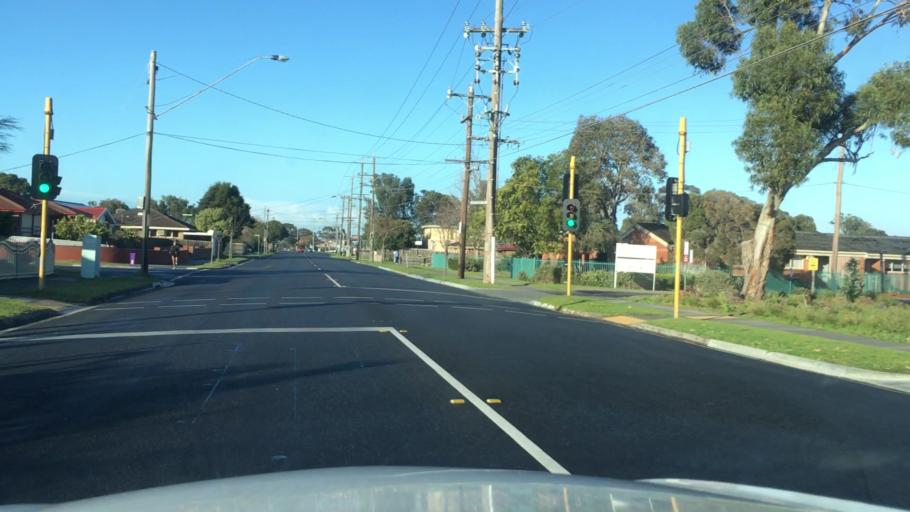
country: AU
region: Victoria
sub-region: Greater Dandenong
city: Keysborough
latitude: -37.9898
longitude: 145.1635
